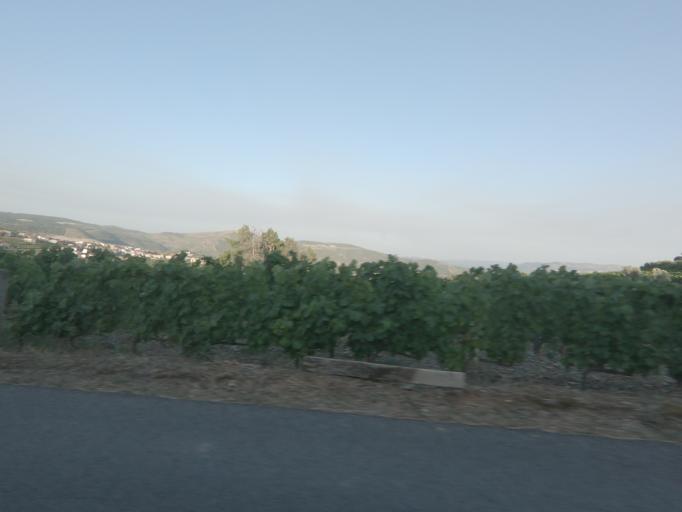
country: PT
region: Vila Real
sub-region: Sabrosa
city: Vilela
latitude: 41.2068
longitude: -7.6746
